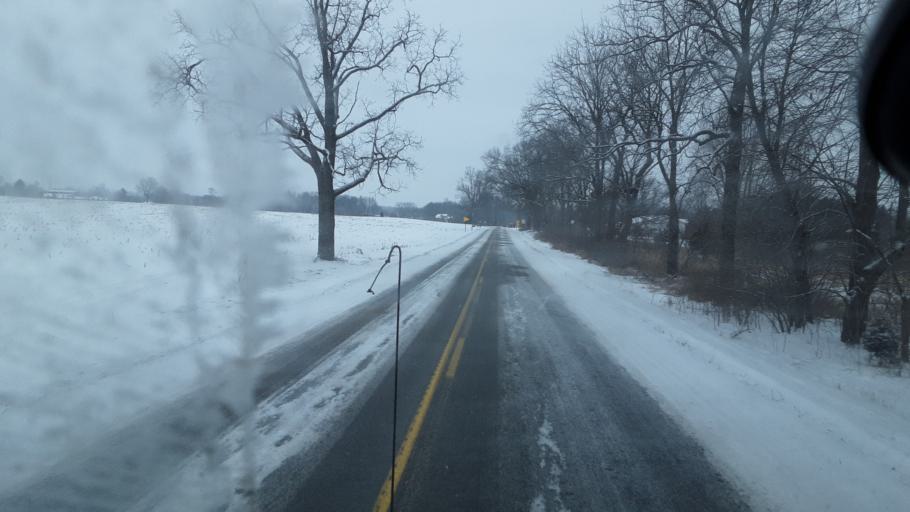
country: US
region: Michigan
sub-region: Ingham County
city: Leslie
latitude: 42.4283
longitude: -84.3168
